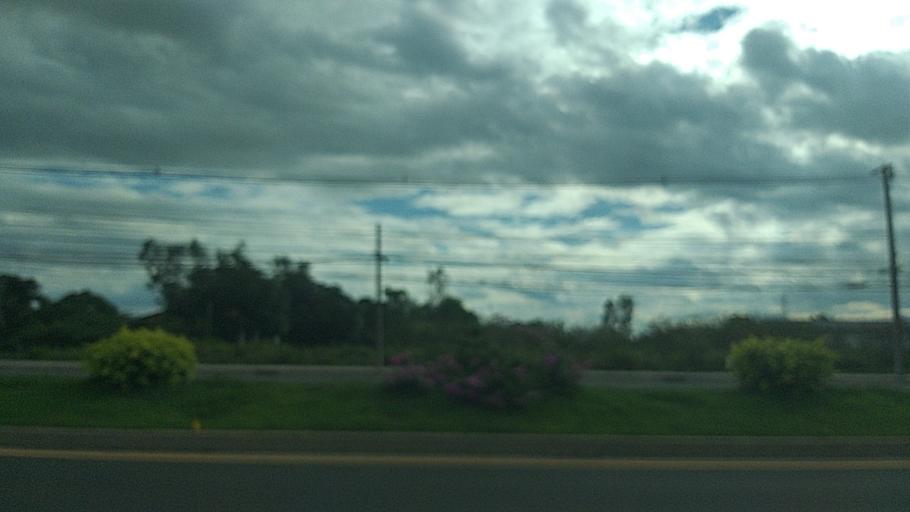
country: TH
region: Surin
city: Prasat
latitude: 14.6248
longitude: 103.4108
